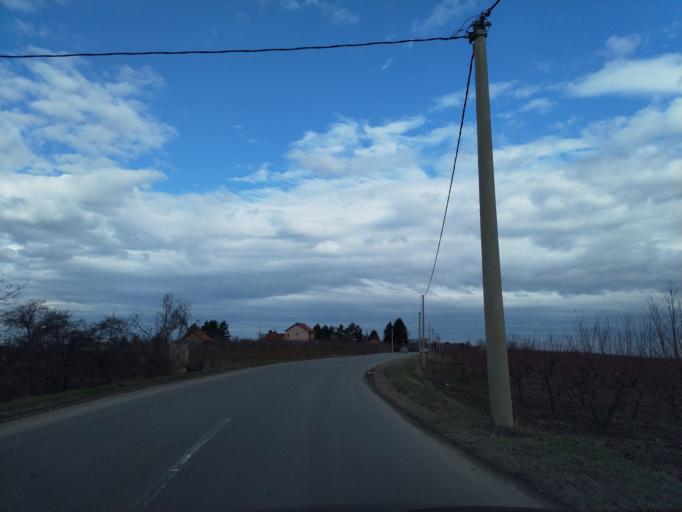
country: RS
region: Central Serbia
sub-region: Belgrade
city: Grocka
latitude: 44.6252
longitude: 20.7432
